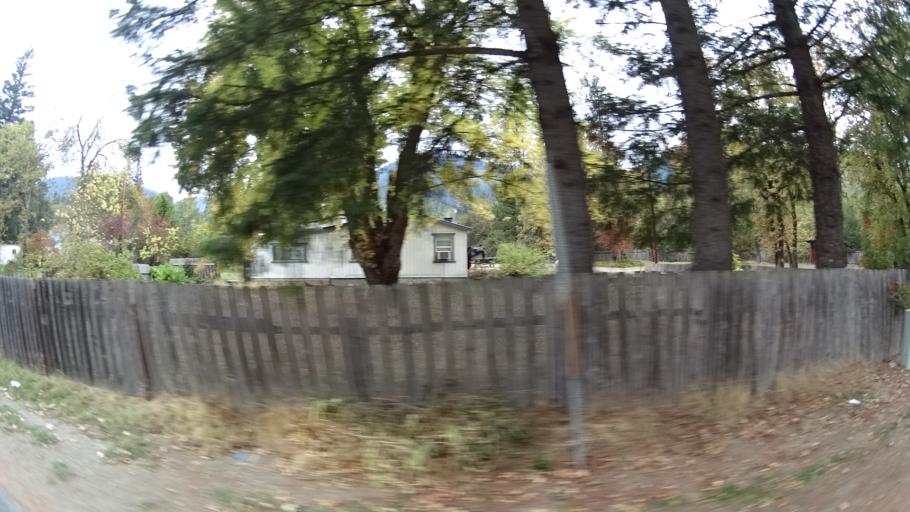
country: US
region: California
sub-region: Siskiyou County
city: Happy Camp
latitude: 41.7843
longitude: -123.3912
